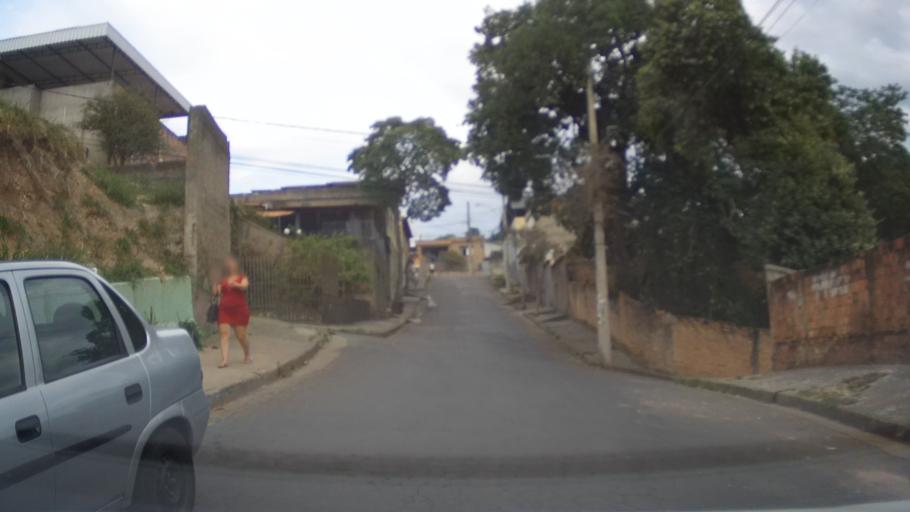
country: BR
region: Minas Gerais
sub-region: Belo Horizonte
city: Belo Horizonte
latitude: -19.8765
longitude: -43.9239
